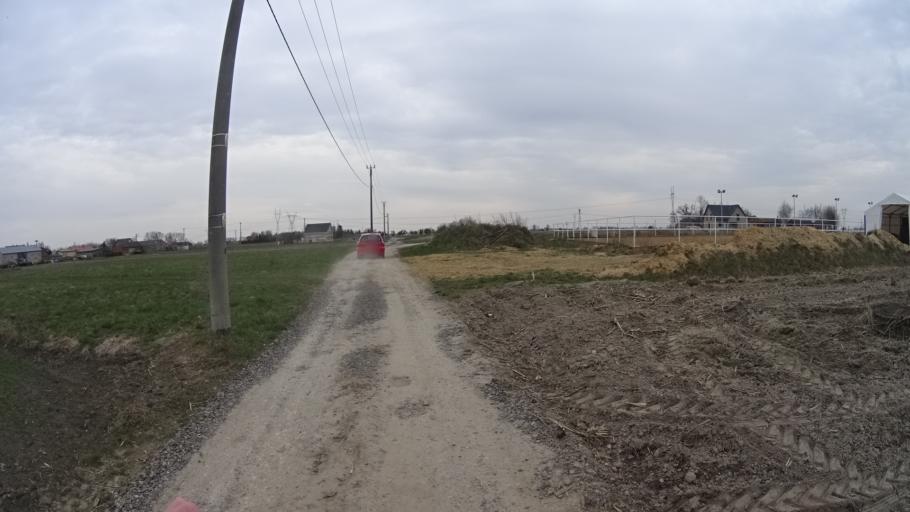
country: PL
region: Masovian Voivodeship
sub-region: Powiat warszawski zachodni
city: Jozefow
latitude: 52.2430
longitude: 20.6886
